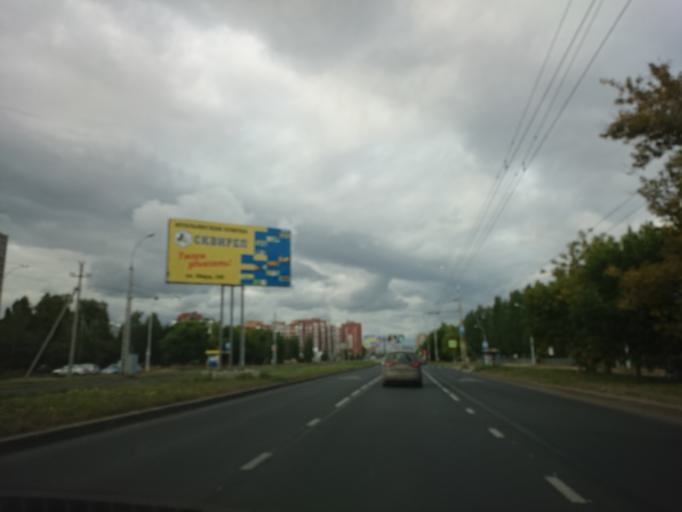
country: RU
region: Samara
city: Tol'yatti
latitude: 53.5103
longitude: 49.3043
